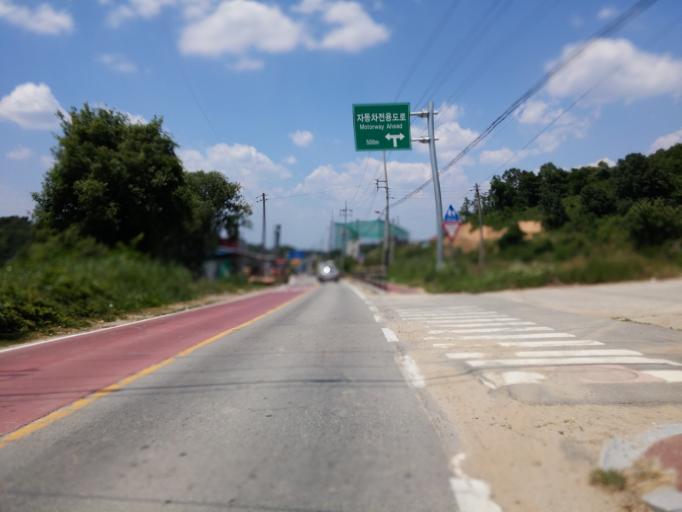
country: KR
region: Chungcheongbuk-do
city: Cheongju-si
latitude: 36.5965
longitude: 127.4416
